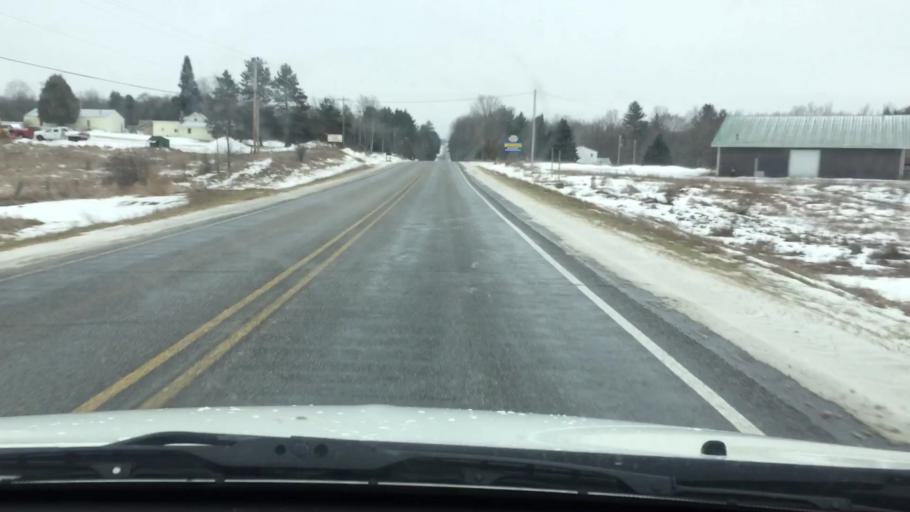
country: US
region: Michigan
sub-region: Wexford County
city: Cadillac
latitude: 44.0623
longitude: -85.4440
